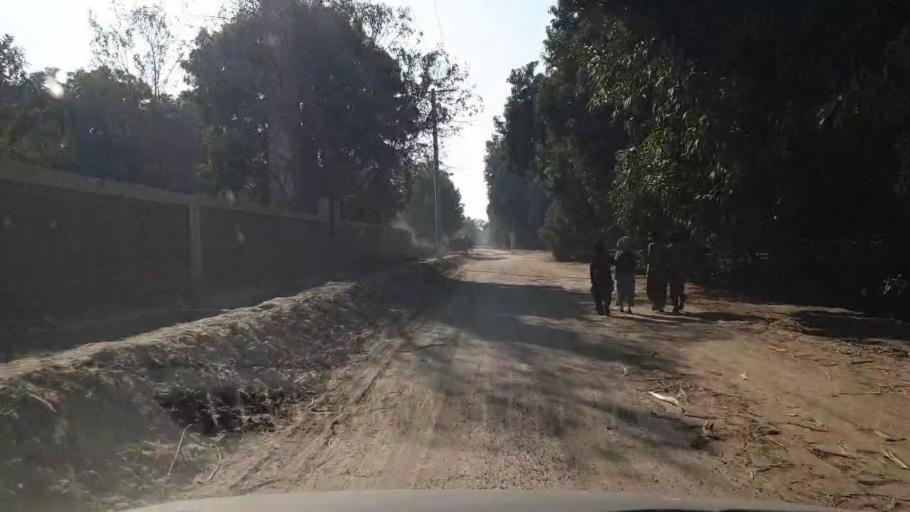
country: PK
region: Sindh
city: Tando Jam
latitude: 25.4404
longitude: 68.6017
